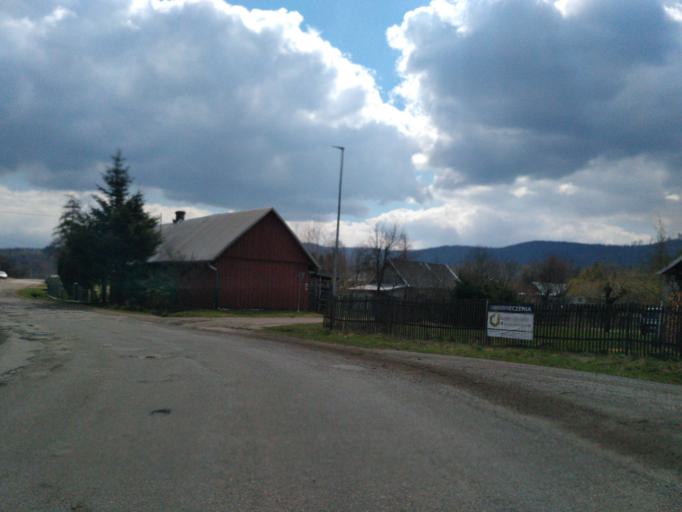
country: PL
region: Subcarpathian Voivodeship
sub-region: Powiat sanocki
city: Sanok
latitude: 49.6115
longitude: 22.2811
